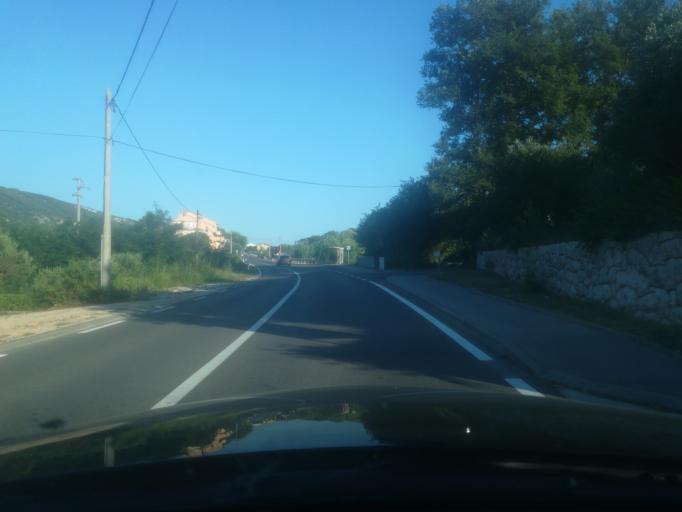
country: HR
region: Primorsko-Goranska
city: Kampor
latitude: 44.7766
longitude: 14.7543
